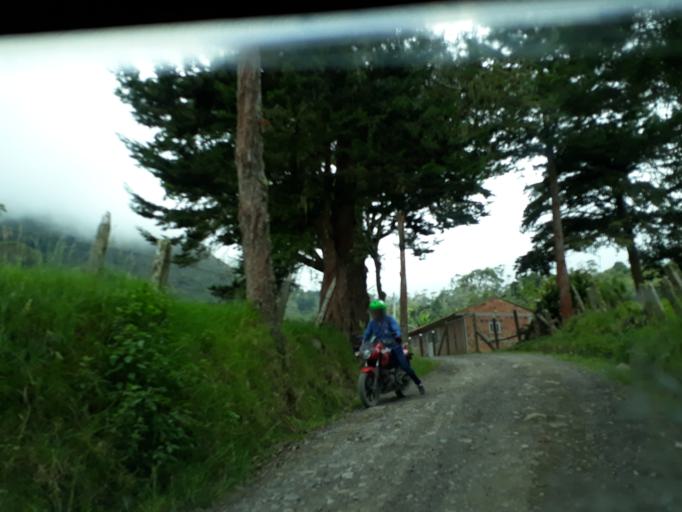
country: CO
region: Cundinamarca
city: Carmen de Carupa
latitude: 5.3822
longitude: -73.9804
